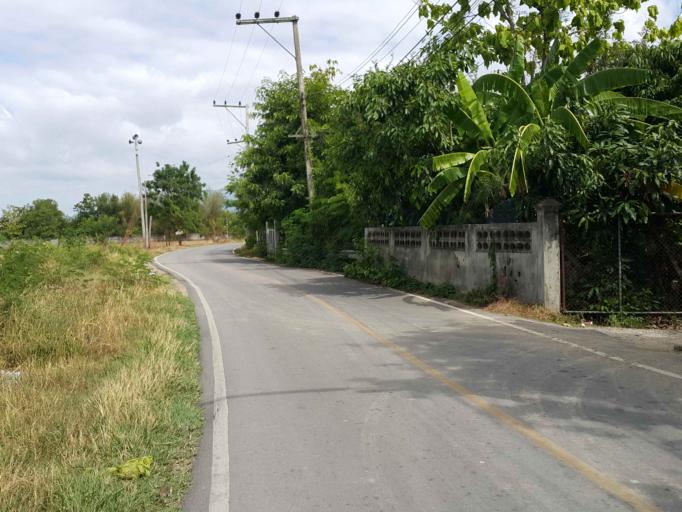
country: TH
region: Chiang Mai
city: San Kamphaeng
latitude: 18.7517
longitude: 99.0871
